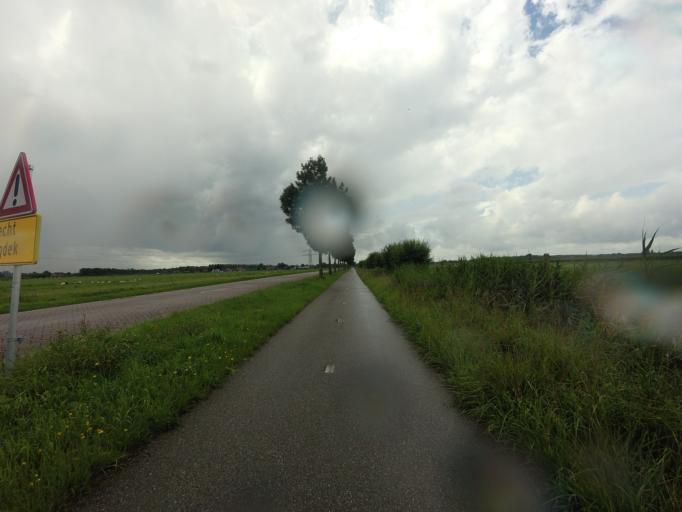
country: NL
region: Utrecht
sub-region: Gemeente Utrecht
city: Utrecht
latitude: 52.1456
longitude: 5.1202
